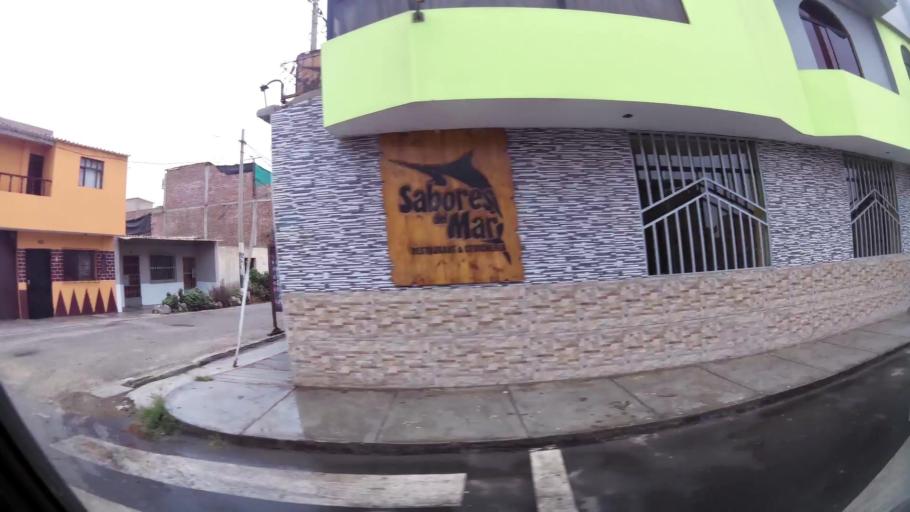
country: PE
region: La Libertad
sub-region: Provincia de Trujillo
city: La Esperanza
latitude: -8.0837
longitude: -79.0479
